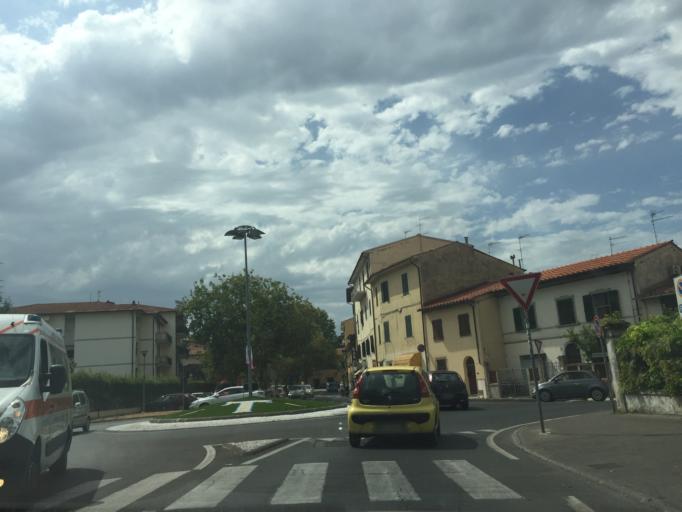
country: IT
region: Tuscany
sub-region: Province of Pisa
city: Pisa
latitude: 43.7256
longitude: 10.4043
